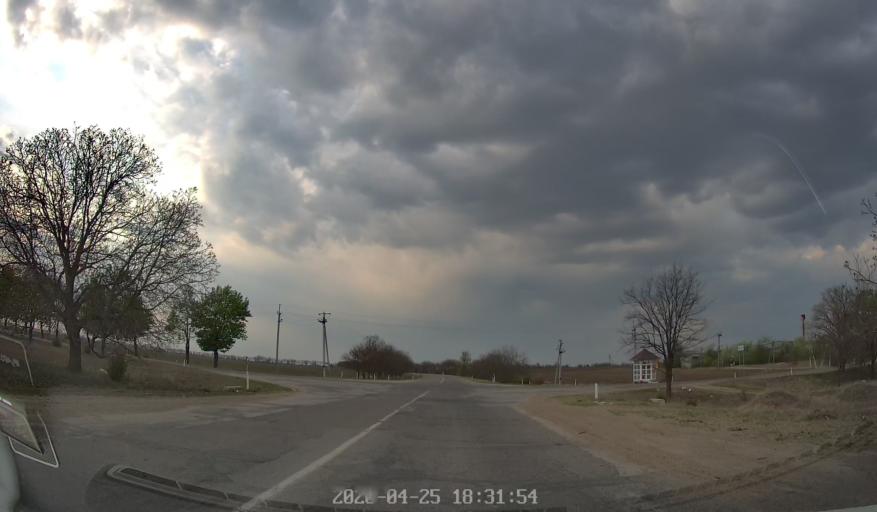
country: MD
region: Criuleni
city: Criuleni
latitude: 47.2227
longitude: 29.1456
